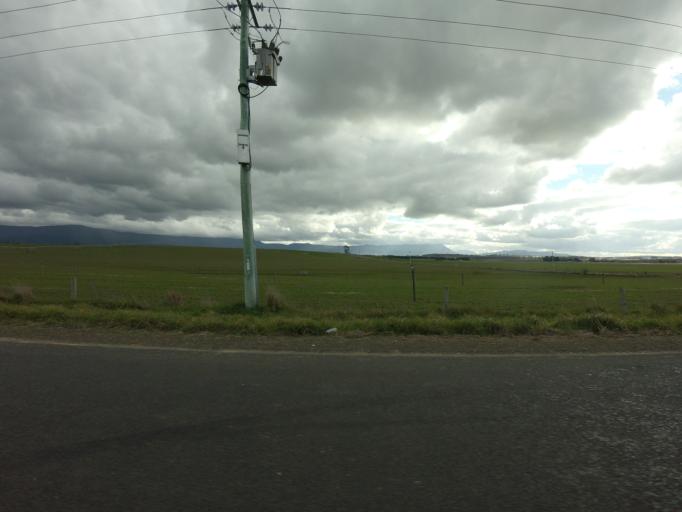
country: AU
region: Tasmania
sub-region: Northern Midlands
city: Longford
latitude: -41.7568
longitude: 147.0825
